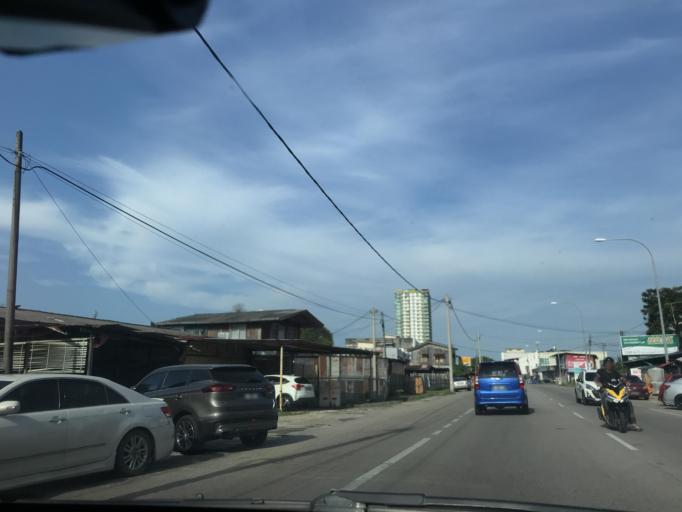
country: MY
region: Kelantan
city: Kota Bharu
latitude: 6.1246
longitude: 102.2644
